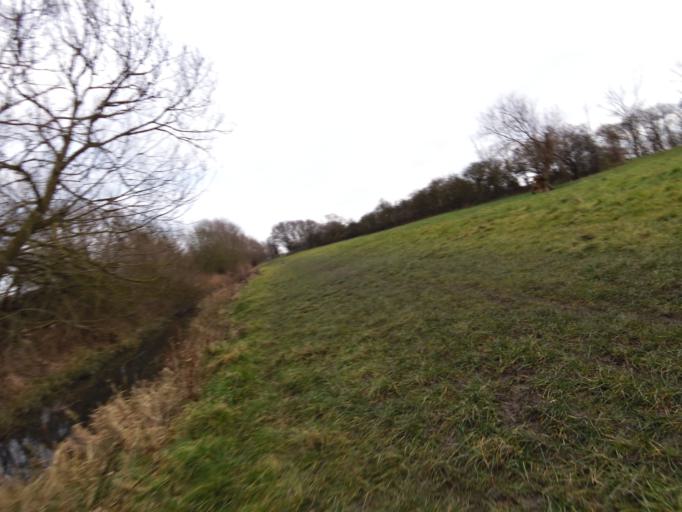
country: GB
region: England
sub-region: Cambridgeshire
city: Waterbeach
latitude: 52.2648
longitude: 0.2188
